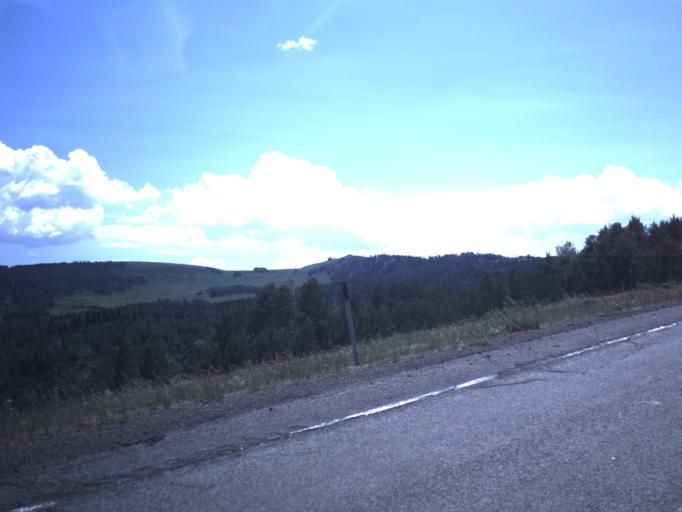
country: US
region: Utah
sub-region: Sanpete County
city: Fairview
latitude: 39.6483
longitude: -111.3288
